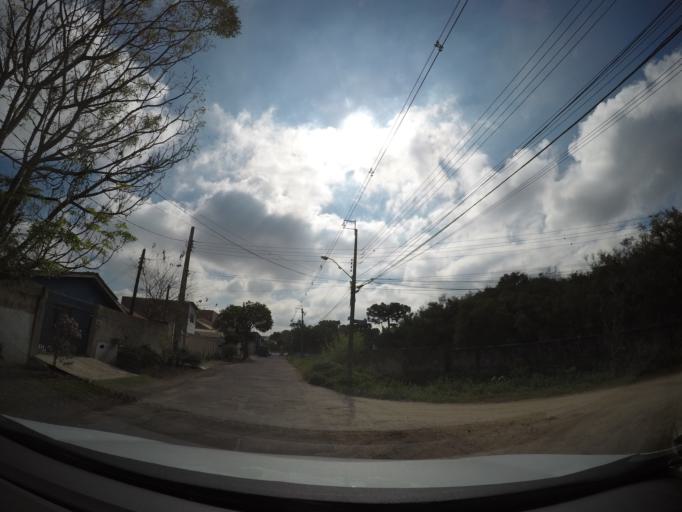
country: BR
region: Parana
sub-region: Sao Jose Dos Pinhais
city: Sao Jose dos Pinhais
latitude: -25.4947
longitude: -49.2204
